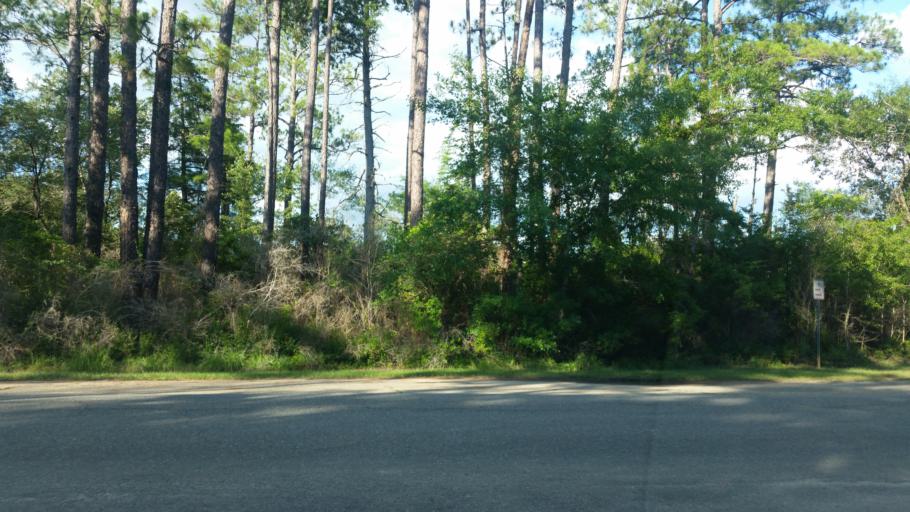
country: US
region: Florida
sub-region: Santa Rosa County
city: East Milton
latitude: 30.7053
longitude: -86.8827
